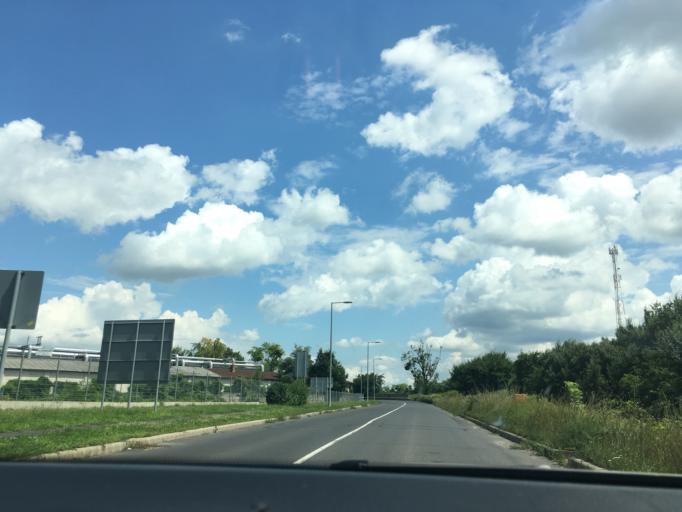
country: HU
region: Borsod-Abauj-Zemplen
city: Satoraljaujhely
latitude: 48.3886
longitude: 21.6618
